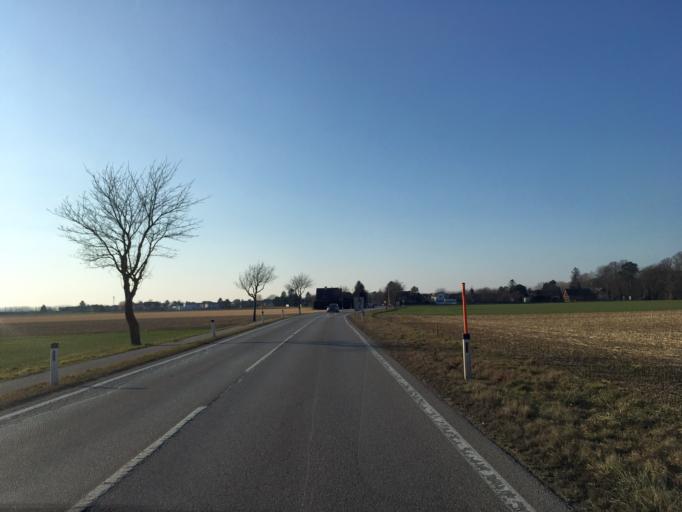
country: AT
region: Lower Austria
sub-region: Politischer Bezirk Tulln
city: Konigstetten
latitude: 48.3300
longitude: 16.1649
